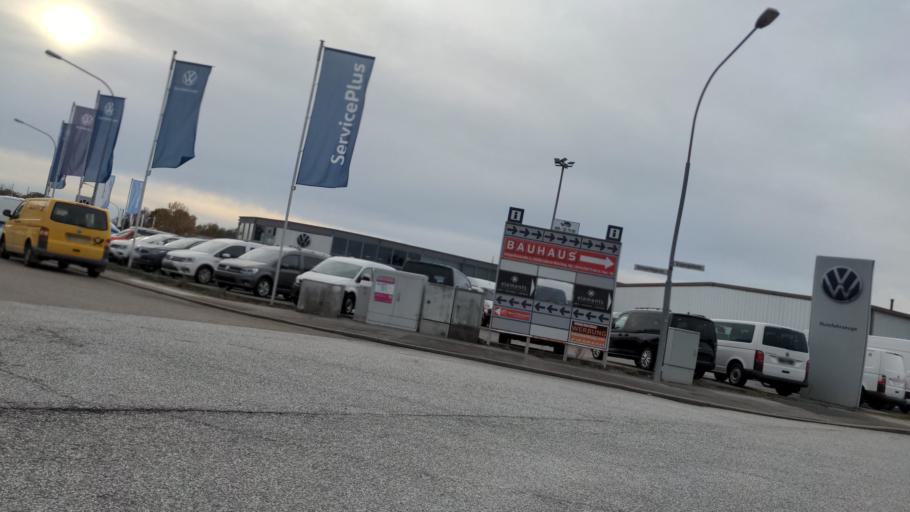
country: DE
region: Schleswig-Holstein
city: Stockelsdorf
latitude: 53.8588
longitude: 10.6370
